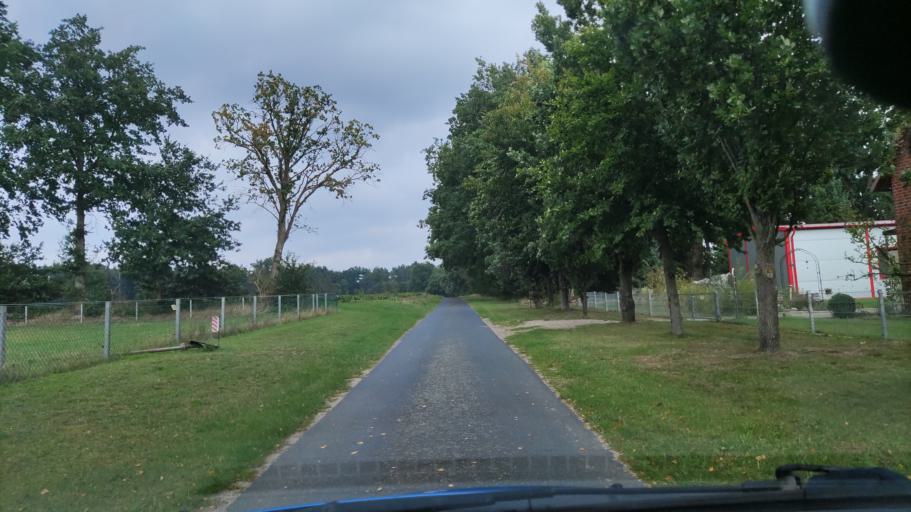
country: DE
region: Lower Saxony
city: Bienenbuttel
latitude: 53.1653
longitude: 10.4992
